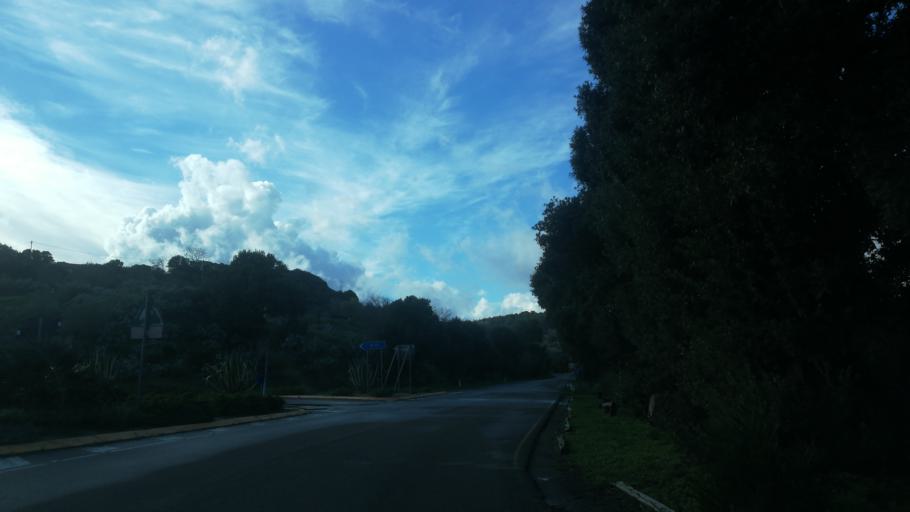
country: IT
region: Sardinia
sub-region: Provincia di Medio Campidano
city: Villanovaforru
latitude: 39.6332
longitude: 8.8637
